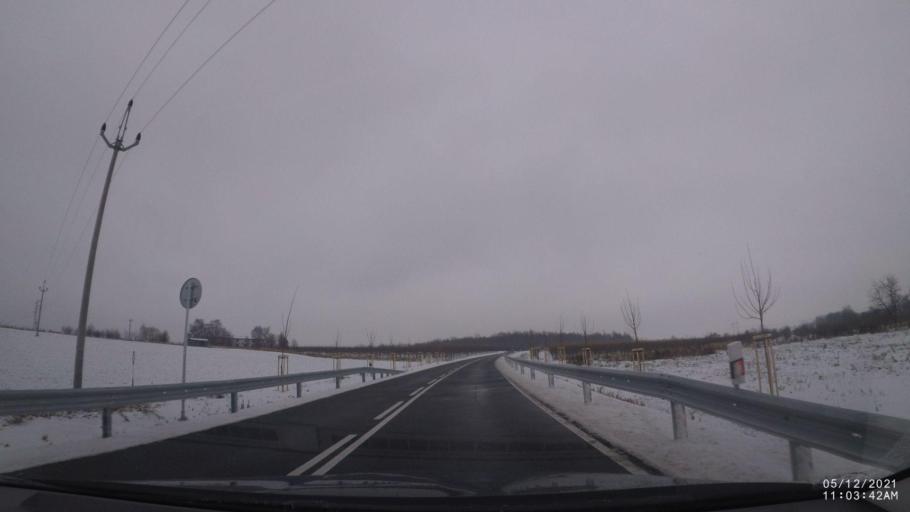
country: CZ
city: Solnice
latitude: 50.1765
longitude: 16.2212
